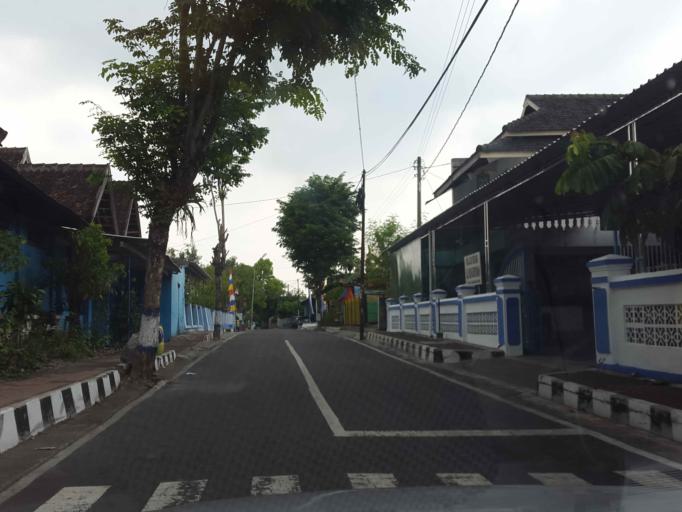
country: ID
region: Central Java
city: Jaten
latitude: -7.5992
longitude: 110.9526
